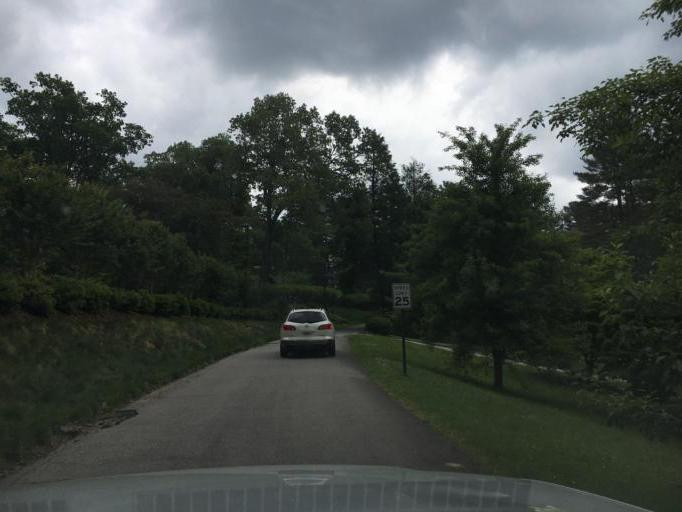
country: US
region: North Carolina
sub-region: Transylvania County
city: Brevard
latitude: 35.2255
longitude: -82.7280
